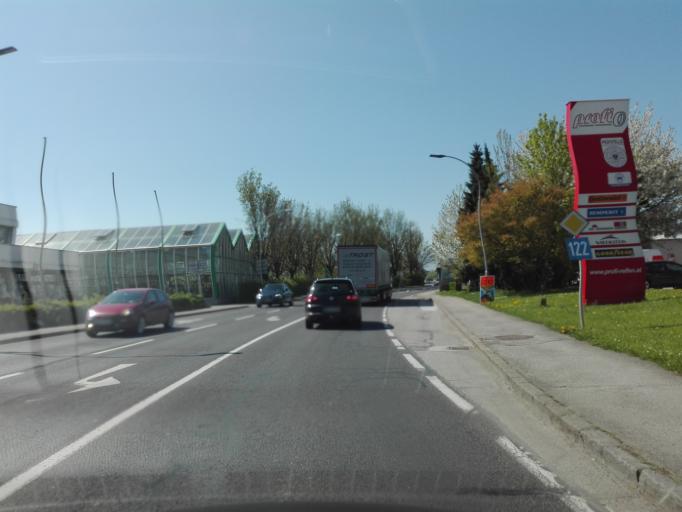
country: AT
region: Upper Austria
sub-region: Steyr Stadt
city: Steyr
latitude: 48.0476
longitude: 14.4140
